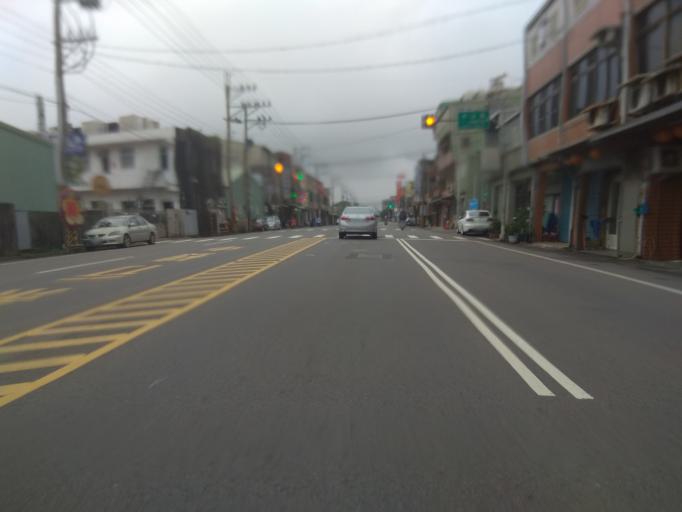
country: TW
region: Taiwan
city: Taoyuan City
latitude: 25.0296
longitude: 121.1060
